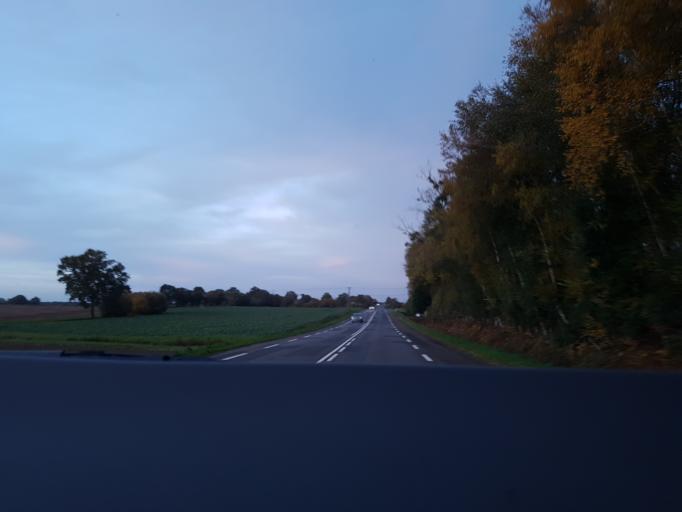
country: FR
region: Pays de la Loire
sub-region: Departement de la Mayenne
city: Cosse-le-Vivien
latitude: 47.9615
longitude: -0.8927
